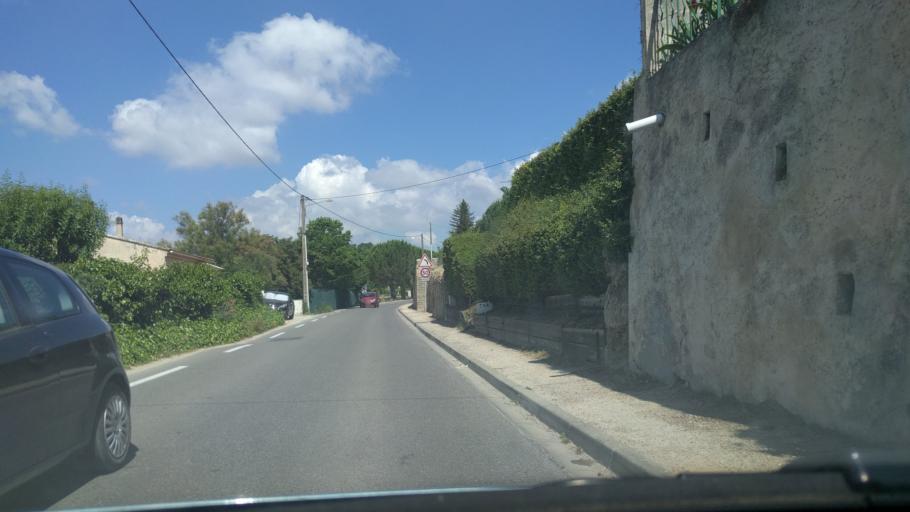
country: FR
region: Provence-Alpes-Cote d'Azur
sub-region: Departement du Vaucluse
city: Grambois
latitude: 43.7309
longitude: 5.5420
